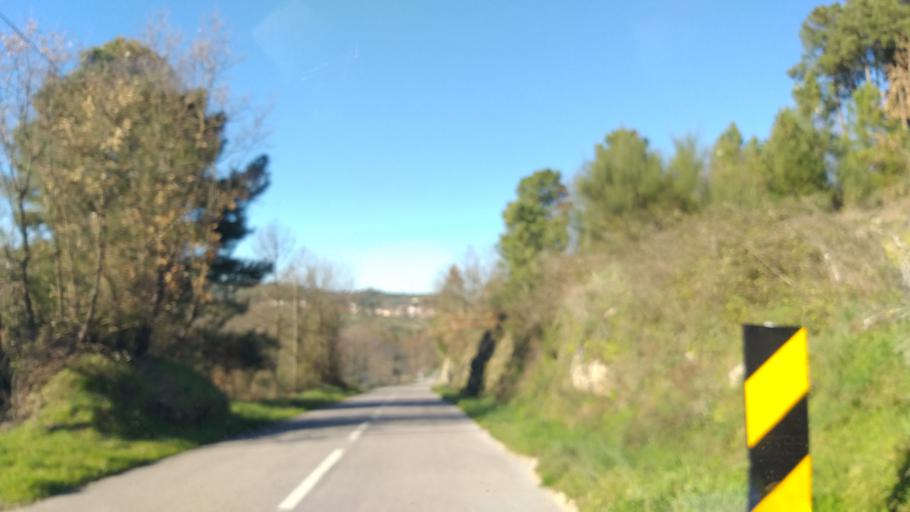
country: PT
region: Guarda
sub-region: Celorico da Beira
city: Celorico da Beira
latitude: 40.5943
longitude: -7.3627
